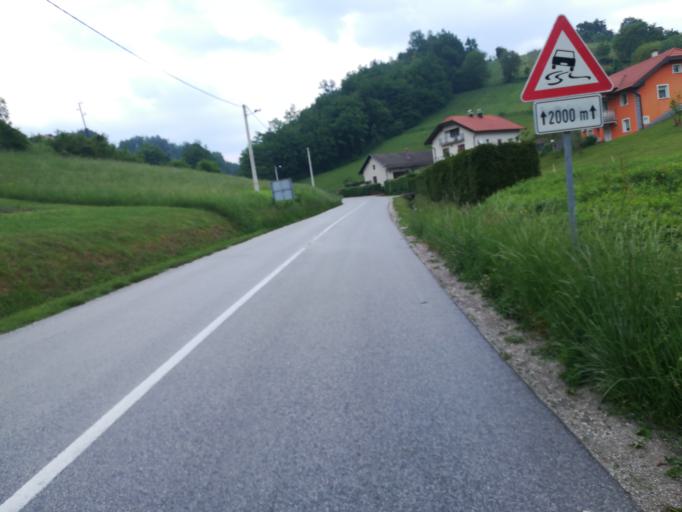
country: HR
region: Varazdinska
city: Klenovnik
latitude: 46.2941
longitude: 16.0201
